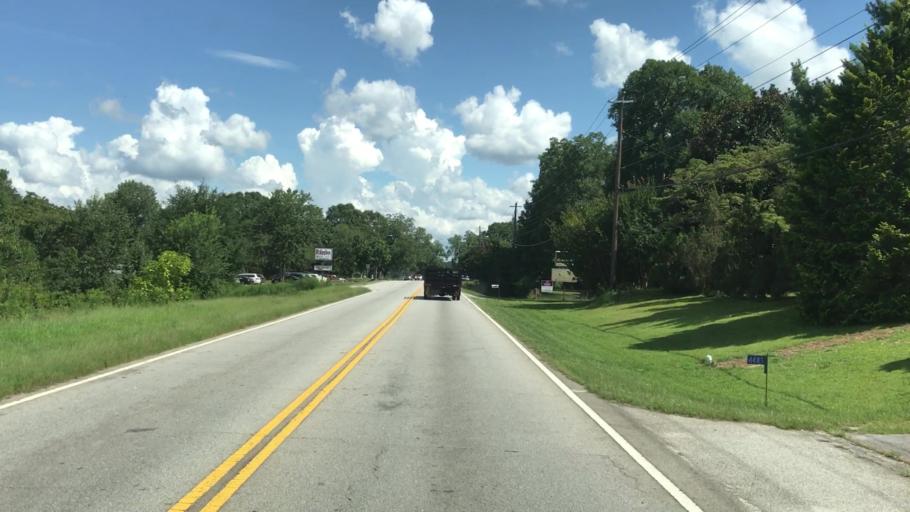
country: US
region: Georgia
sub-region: Walton County
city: Loganville
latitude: 33.8383
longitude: -83.8931
